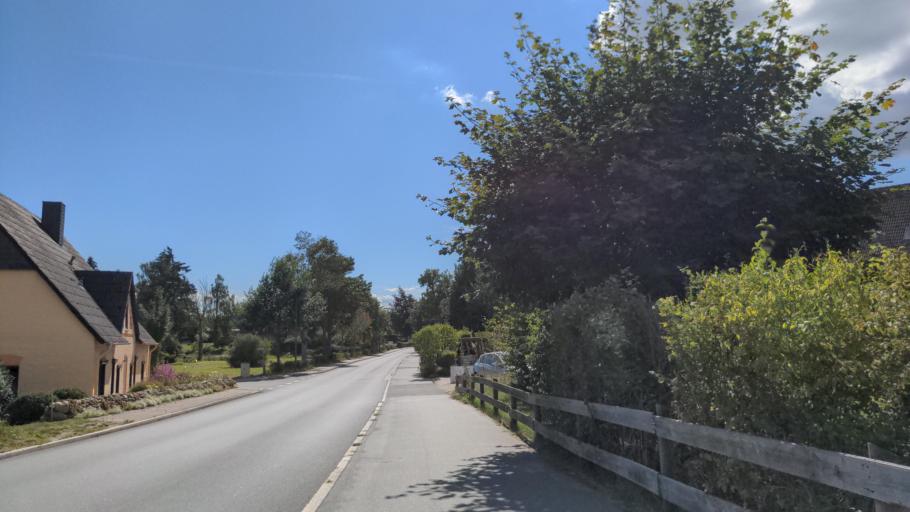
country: DE
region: Schleswig-Holstein
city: Kasseedorf
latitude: 54.1674
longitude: 10.7241
